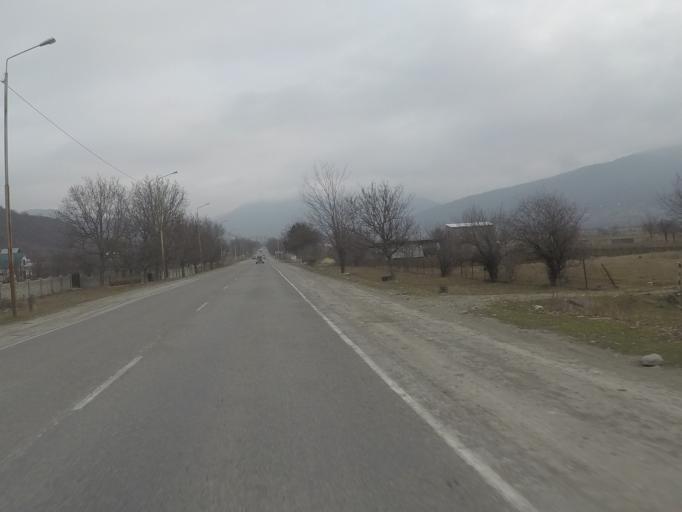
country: GE
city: Zhinvali
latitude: 42.0849
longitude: 44.7554
